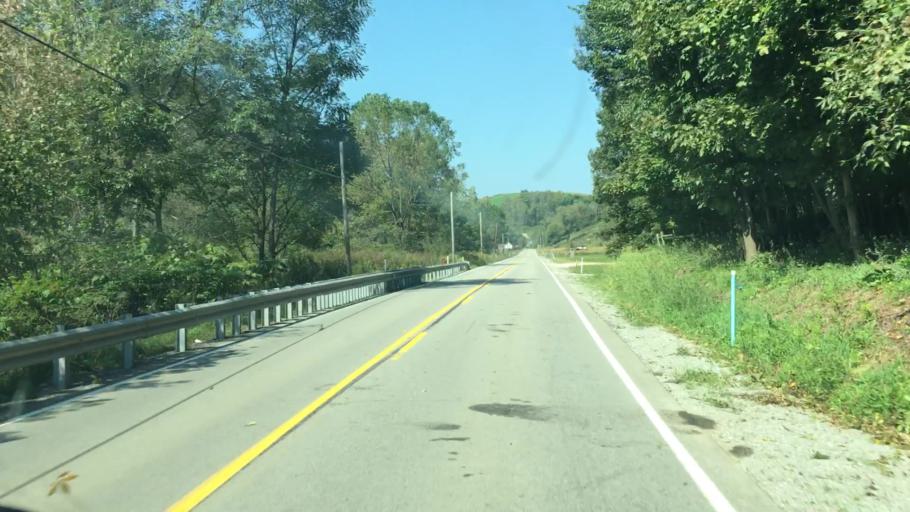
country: US
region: Pennsylvania
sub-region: Greene County
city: Waynesburg
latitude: 39.9503
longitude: -80.3001
